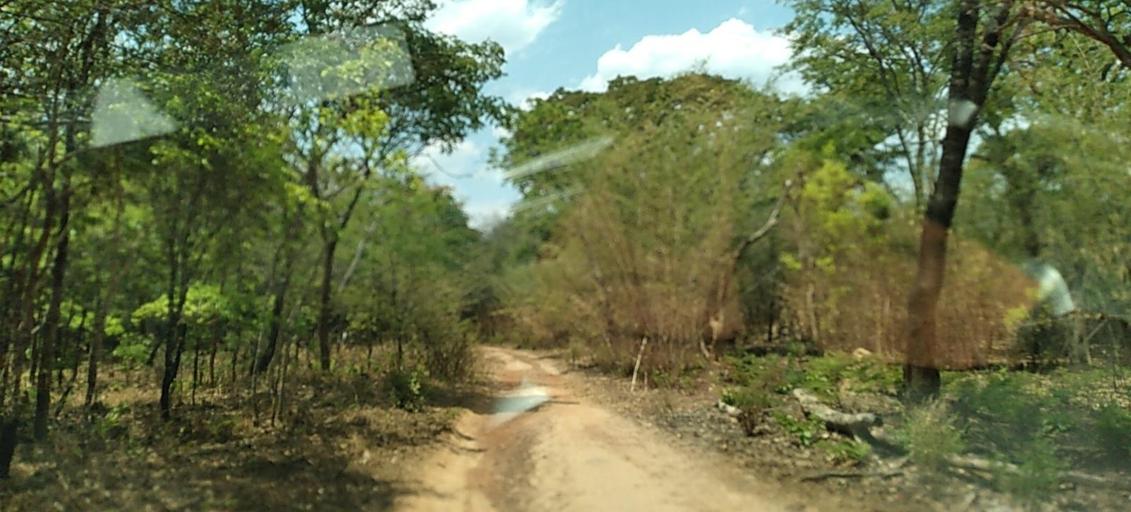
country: ZM
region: Copperbelt
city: Chililabombwe
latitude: -12.4803
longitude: 27.6441
